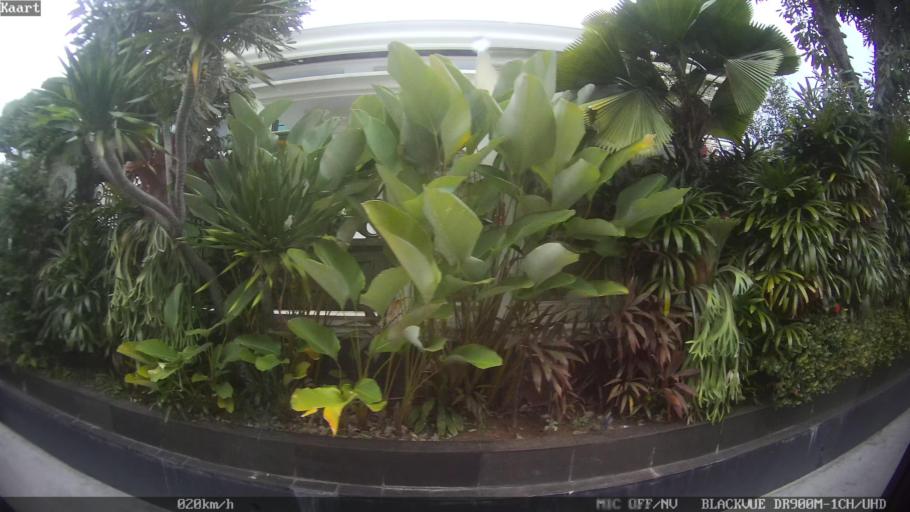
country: ID
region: Lampung
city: Bandarlampung
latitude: -5.4290
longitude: 105.2737
